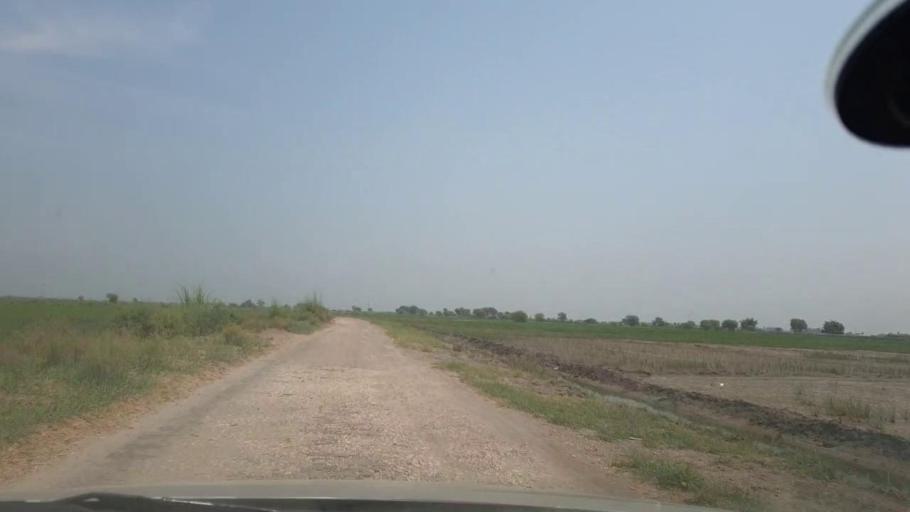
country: PK
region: Sindh
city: Jacobabad
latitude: 28.1396
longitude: 68.3660
